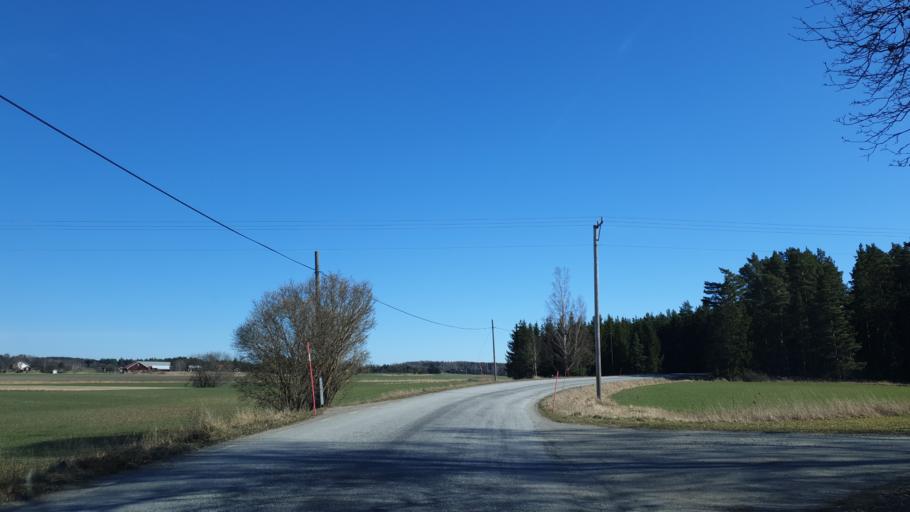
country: SE
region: Uppsala
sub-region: Enkopings Kommun
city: Dalby
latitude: 59.5722
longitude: 17.2990
